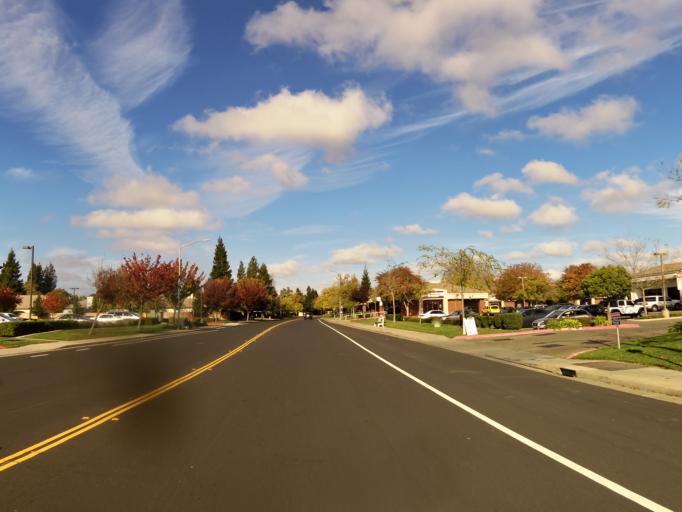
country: US
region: California
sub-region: Sacramento County
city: Elk Grove
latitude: 38.4094
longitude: -121.3956
